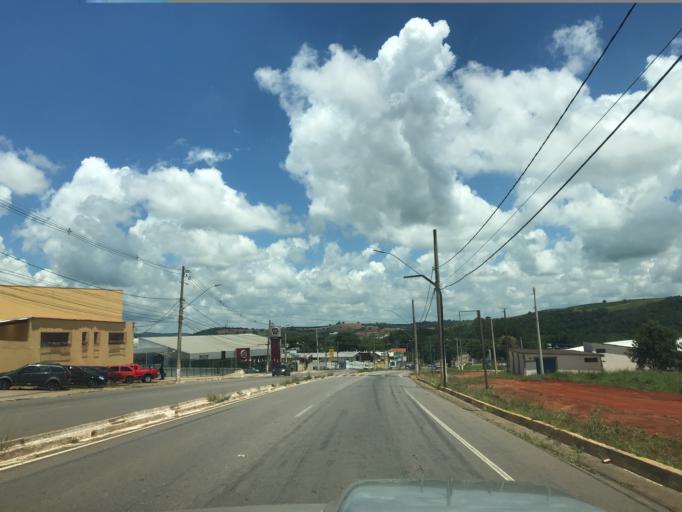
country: BR
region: Minas Gerais
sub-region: Tres Coracoes
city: Tres Coracoes
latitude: -21.6652
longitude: -45.2785
